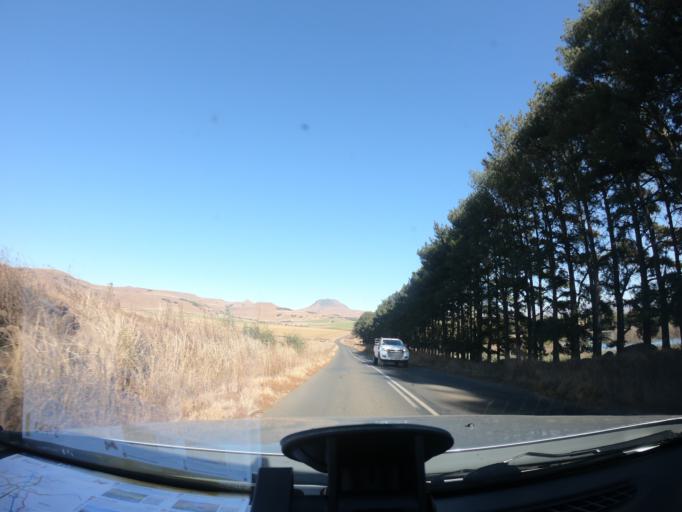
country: ZA
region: KwaZulu-Natal
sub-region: uMgungundlovu District Municipality
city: Mooirivier
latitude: -29.3306
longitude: 29.8213
